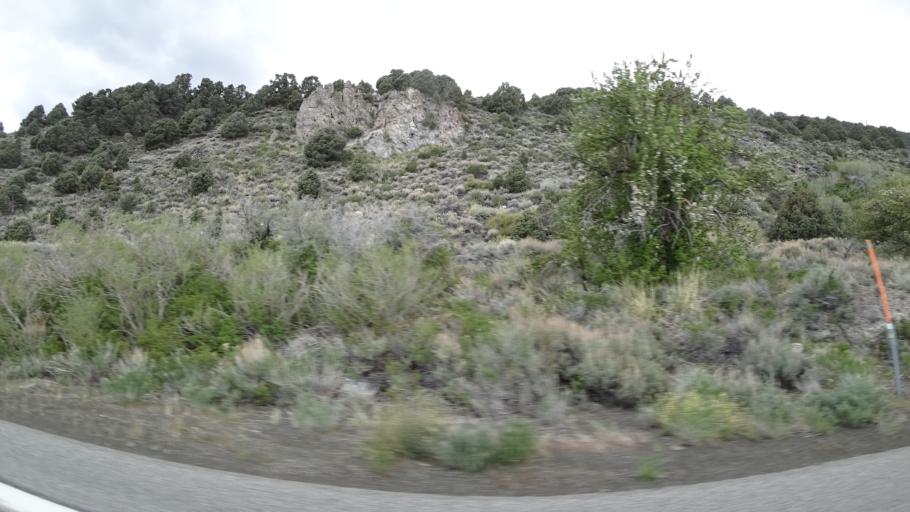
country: US
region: California
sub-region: Mono County
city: Bridgeport
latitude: 38.0043
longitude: -119.1536
